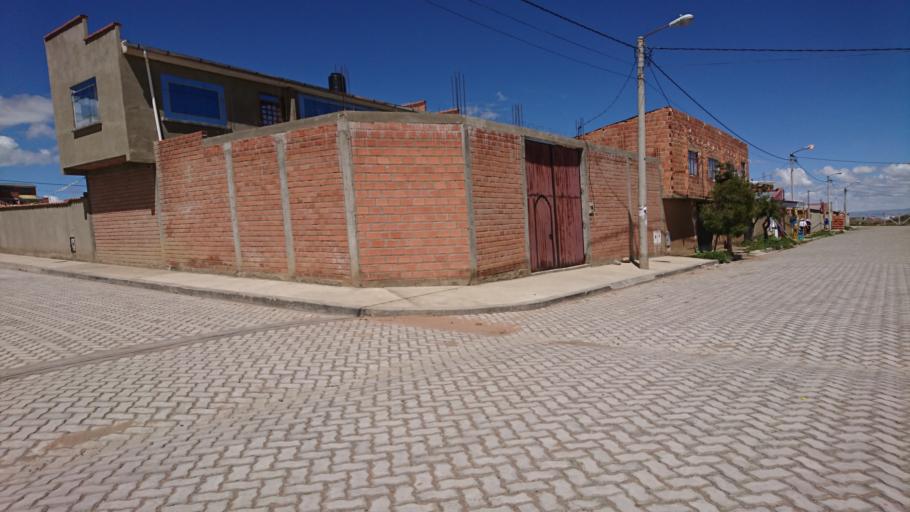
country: BO
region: La Paz
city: La Paz
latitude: -16.5024
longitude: -68.1881
